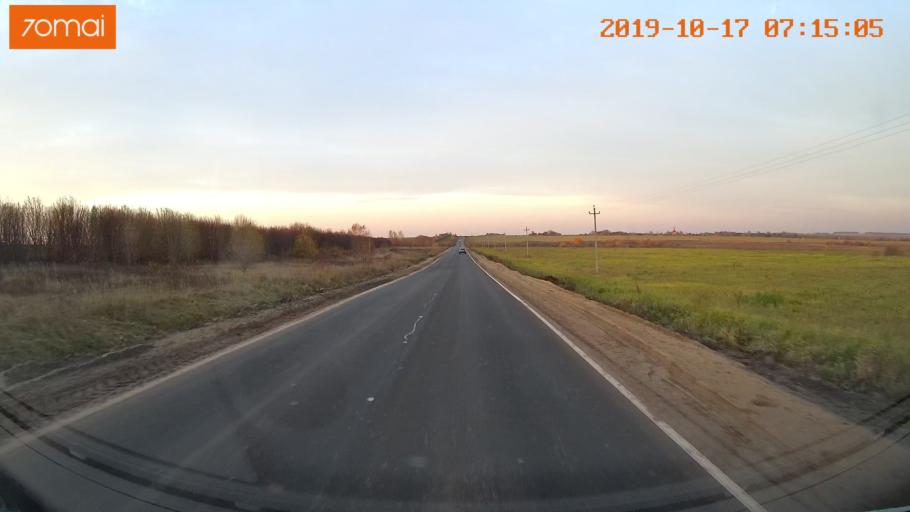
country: RU
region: Vladimir
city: Suzdal'
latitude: 56.3842
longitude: 40.2748
